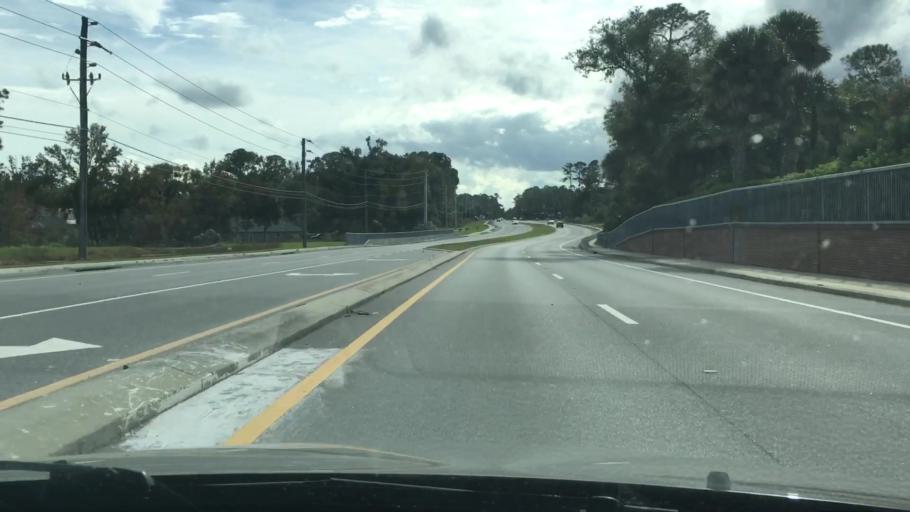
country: US
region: Florida
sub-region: Volusia County
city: Ormond Beach
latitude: 29.2581
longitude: -81.1291
